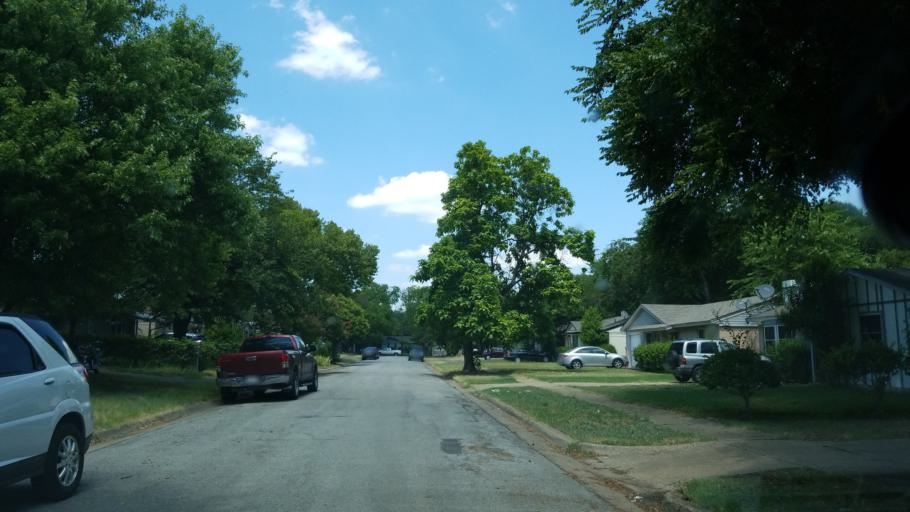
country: US
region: Texas
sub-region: Dallas County
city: Duncanville
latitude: 32.6702
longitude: -96.8973
